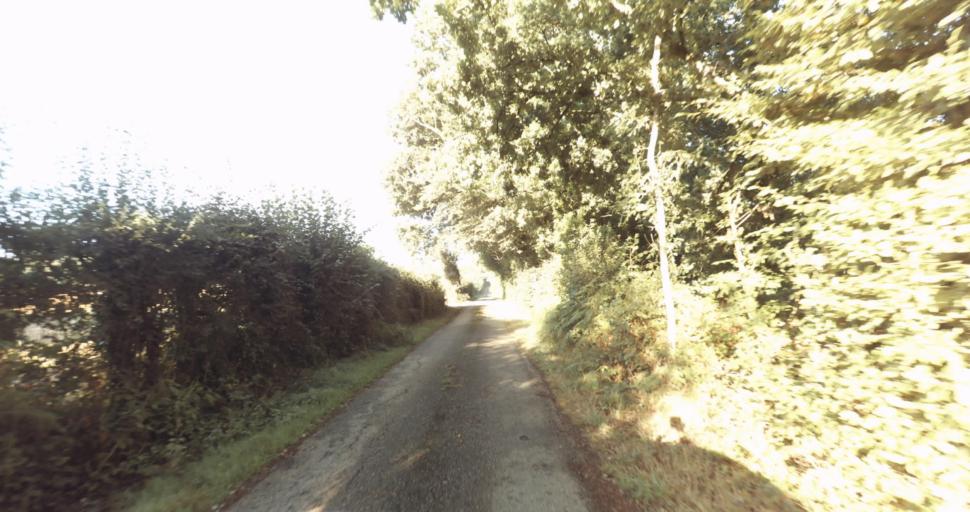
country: FR
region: Lower Normandy
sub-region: Departement de l'Orne
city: Vimoutiers
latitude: 48.9149
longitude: 0.1594
